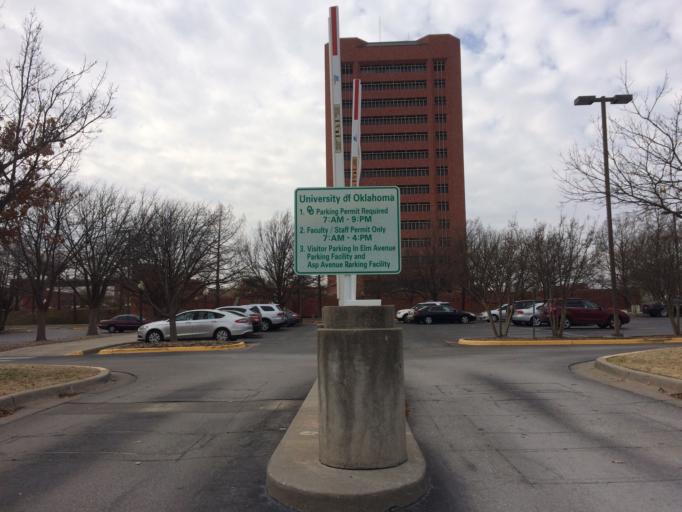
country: US
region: Oklahoma
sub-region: Cleveland County
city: Norman
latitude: 35.2106
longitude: -97.4390
